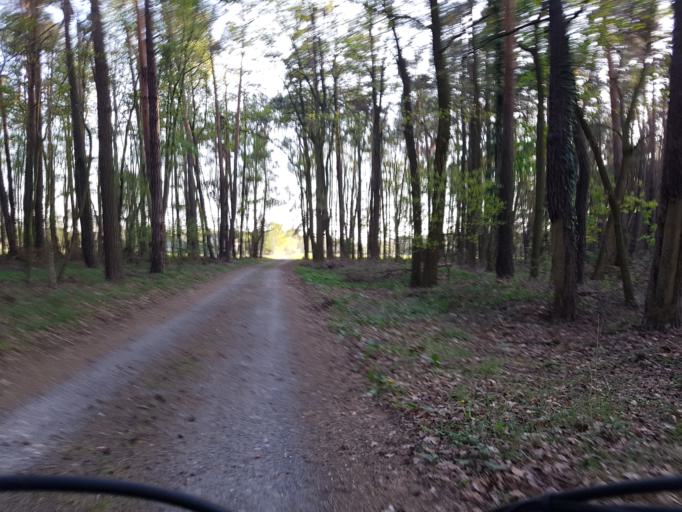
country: DE
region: Brandenburg
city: Schilda
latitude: 51.5955
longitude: 13.3665
